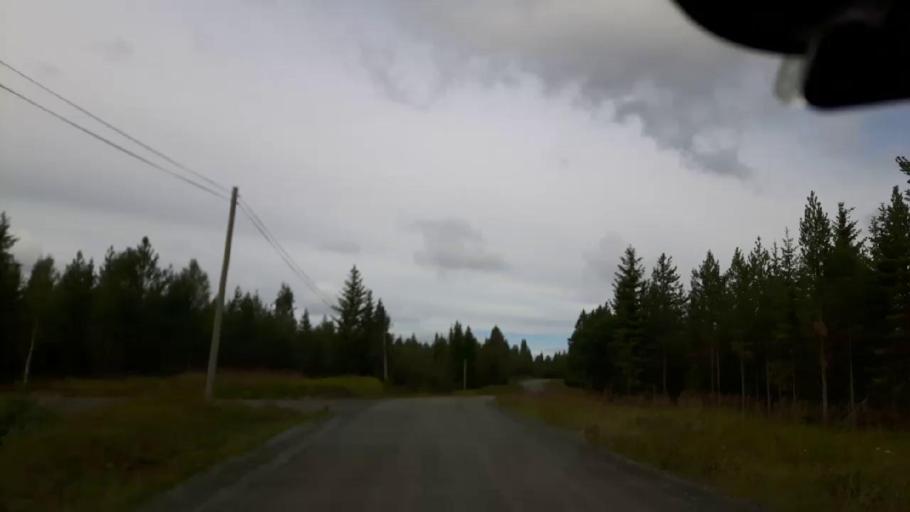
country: SE
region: Jaemtland
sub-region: Krokoms Kommun
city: Valla
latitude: 63.4156
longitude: 14.0839
